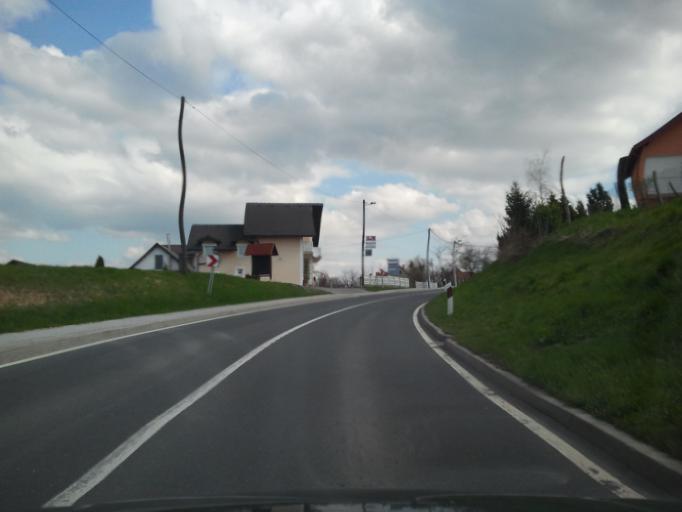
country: HR
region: Grad Zagreb
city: Horvati
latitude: 45.6955
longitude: 15.7493
